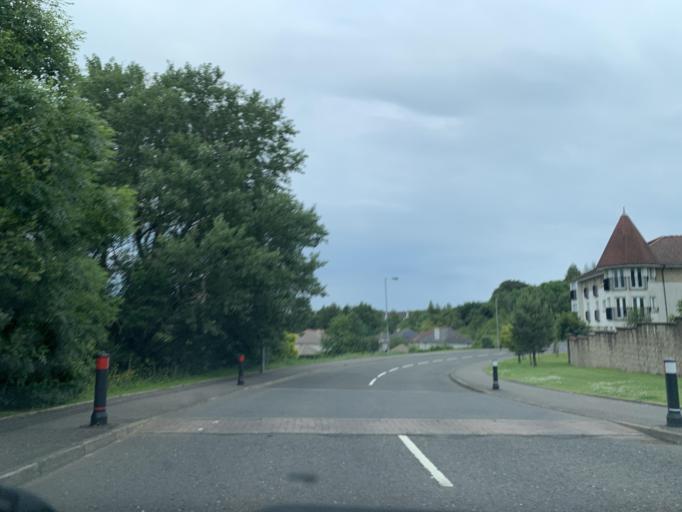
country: GB
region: Scotland
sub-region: East Renfrewshire
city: Newton Mearns
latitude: 55.7706
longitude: -4.3516
